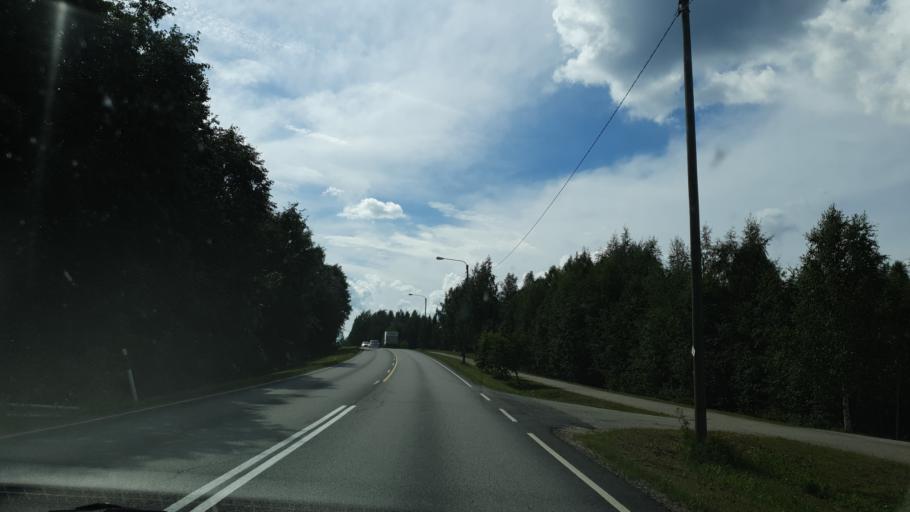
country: FI
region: Kainuu
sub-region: Kajaani
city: Sotkamo
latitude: 64.1685
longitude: 28.4484
